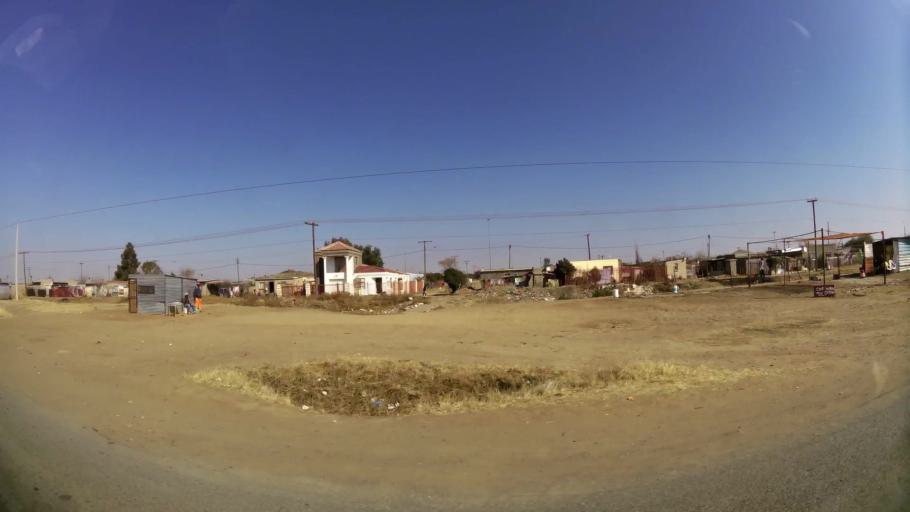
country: ZA
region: Orange Free State
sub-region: Mangaung Metropolitan Municipality
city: Bloemfontein
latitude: -29.1650
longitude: 26.2584
